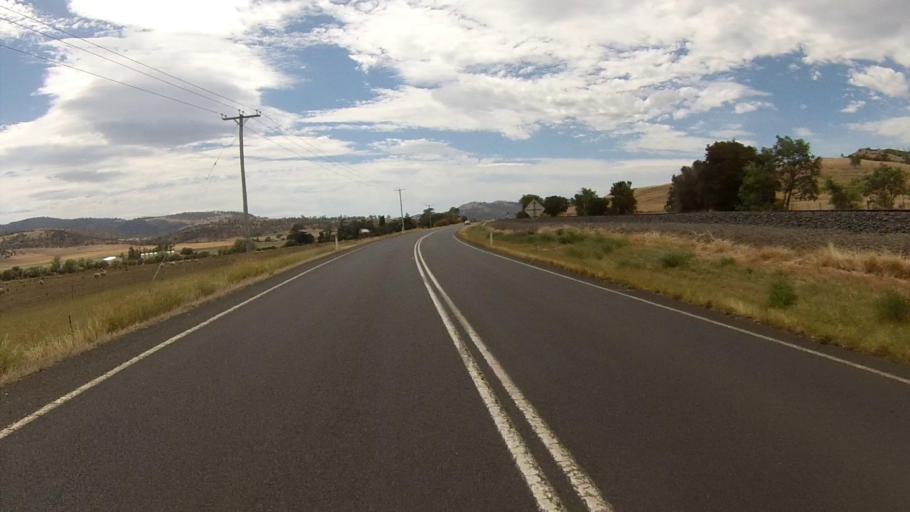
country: AU
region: Tasmania
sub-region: Brighton
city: Bridgewater
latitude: -42.6909
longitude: 147.2994
